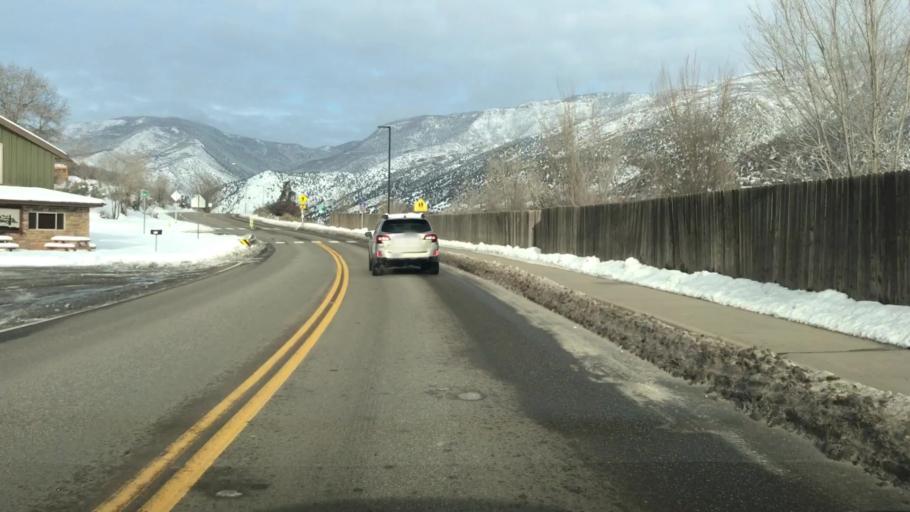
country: US
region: Colorado
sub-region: Garfield County
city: Glenwood Springs
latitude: 39.5480
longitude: -107.3330
